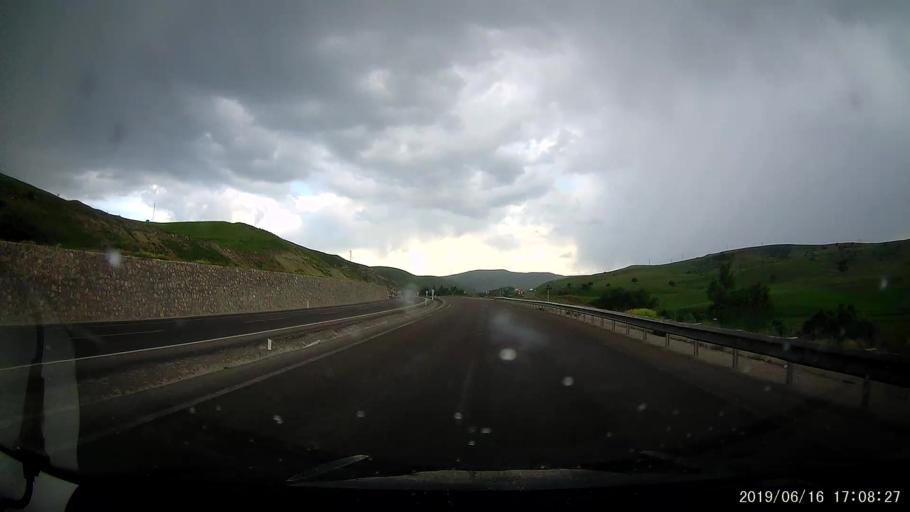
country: TR
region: Erzurum
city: Askale
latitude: 39.9089
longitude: 40.6609
